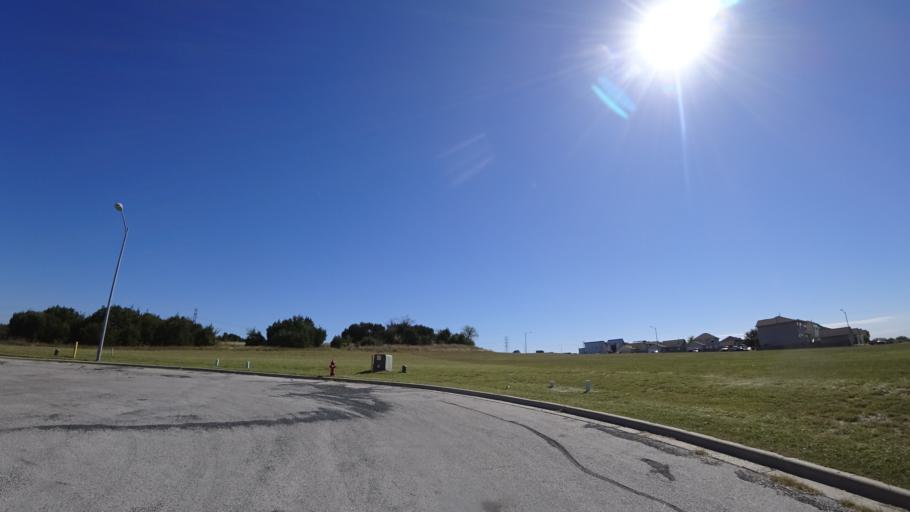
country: US
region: Texas
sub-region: Travis County
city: Hornsby Bend
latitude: 30.2955
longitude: -97.6420
